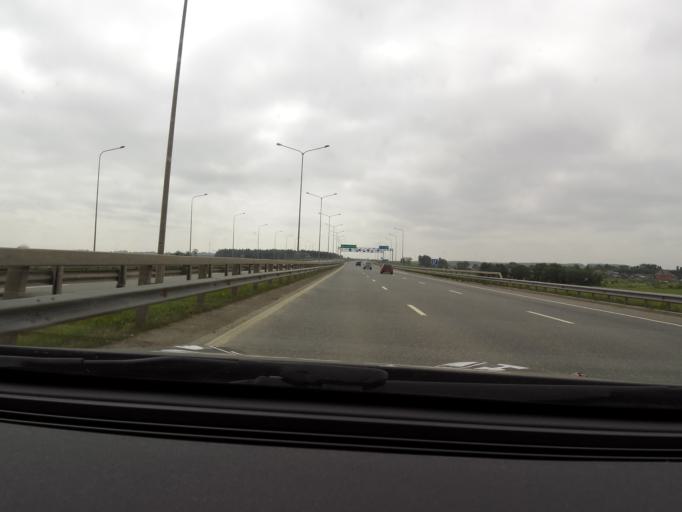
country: RU
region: Perm
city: Froly
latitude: 57.8859
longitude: 56.2665
